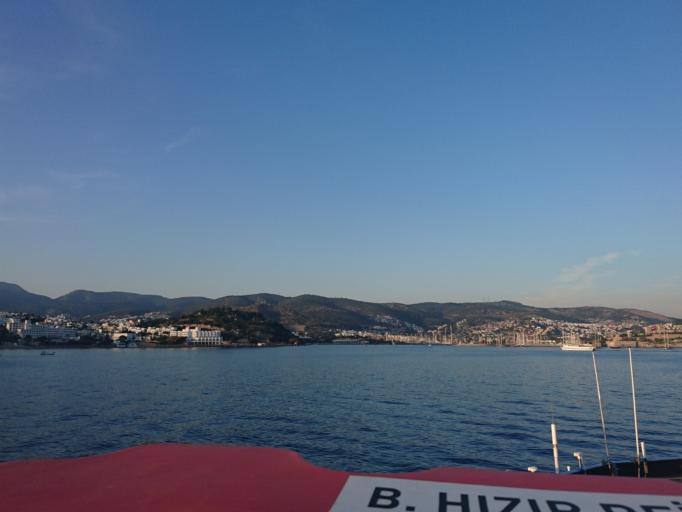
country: TR
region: Mugla
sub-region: Bodrum
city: Bodrum
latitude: 37.0215
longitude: 27.4206
